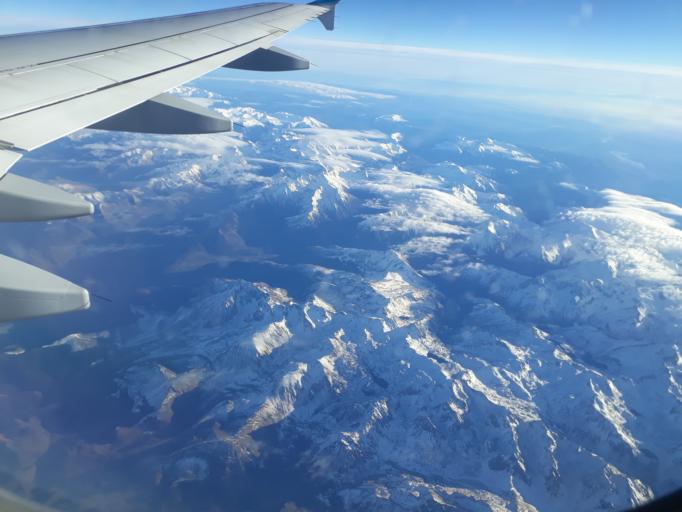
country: FR
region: Midi-Pyrenees
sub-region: Departement des Hautes-Pyrenees
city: Campan
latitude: 42.9992
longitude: 0.1356
